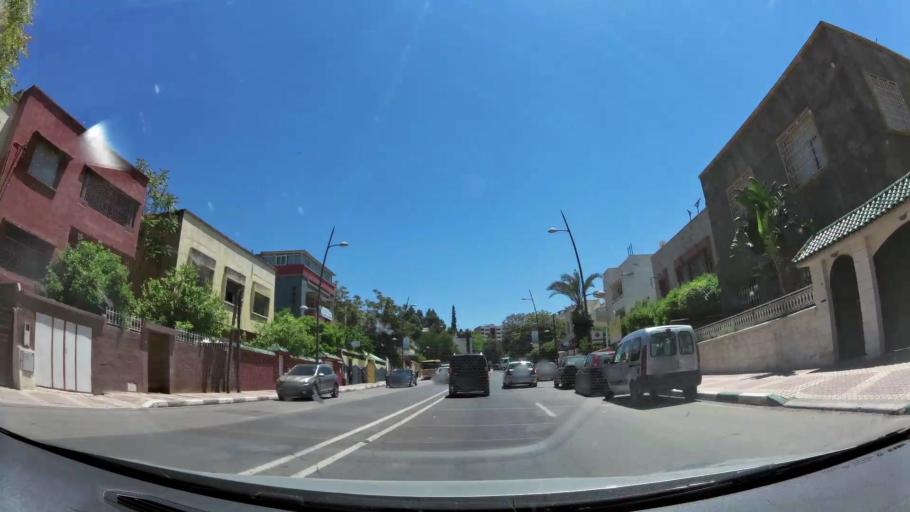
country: MA
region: Meknes-Tafilalet
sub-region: Meknes
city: Meknes
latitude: 33.9027
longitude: -5.5548
